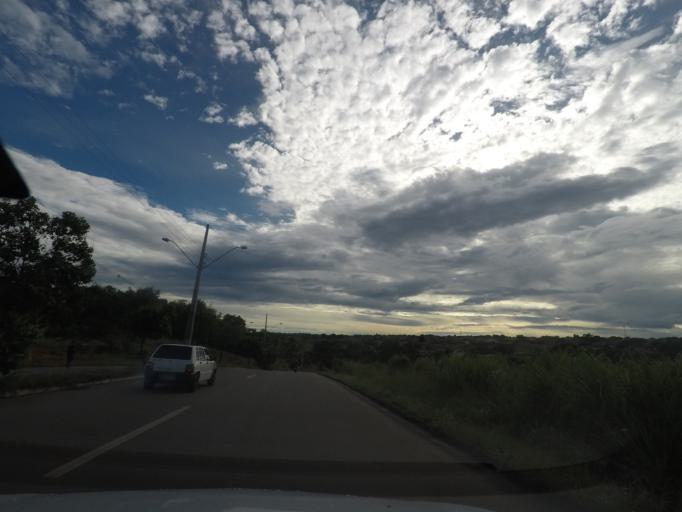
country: BR
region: Goias
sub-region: Aparecida De Goiania
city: Aparecida de Goiania
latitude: -16.7850
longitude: -49.3792
